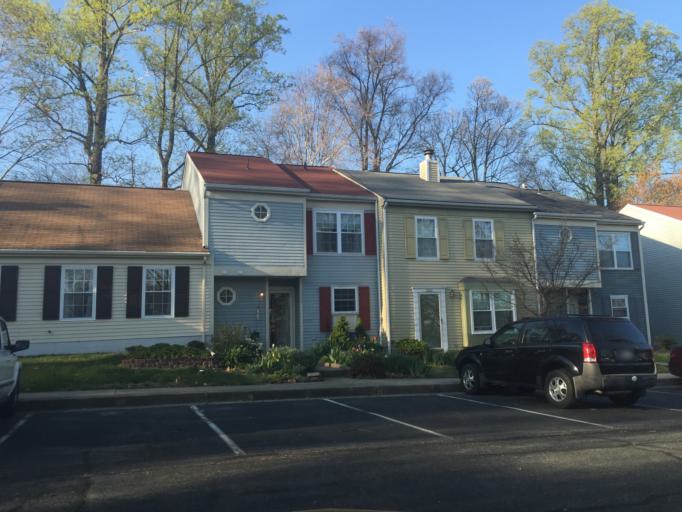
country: US
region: Maryland
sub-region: Harford County
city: Riverside
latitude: 39.4764
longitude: -76.2422
